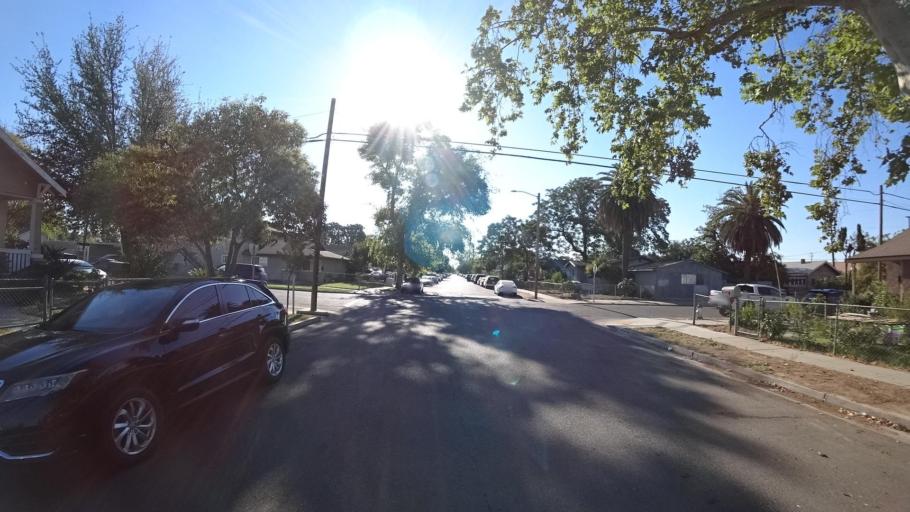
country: US
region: California
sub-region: Fresno County
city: Fresno
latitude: 36.7515
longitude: -119.7857
